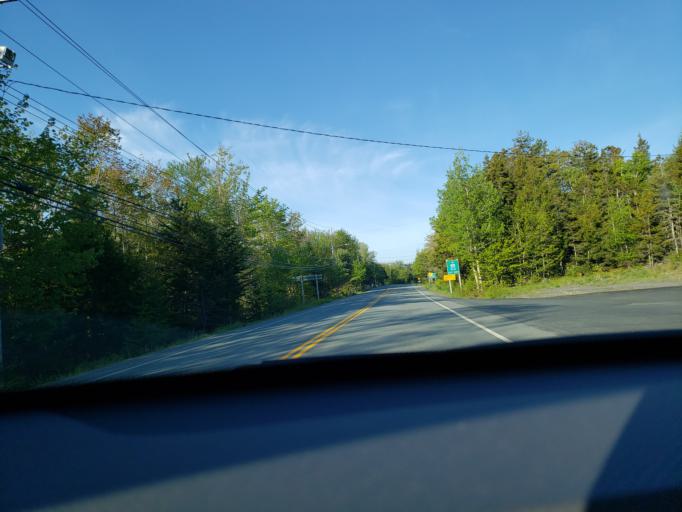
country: CA
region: Nova Scotia
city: Cole Harbour
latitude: 44.7240
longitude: -63.3966
